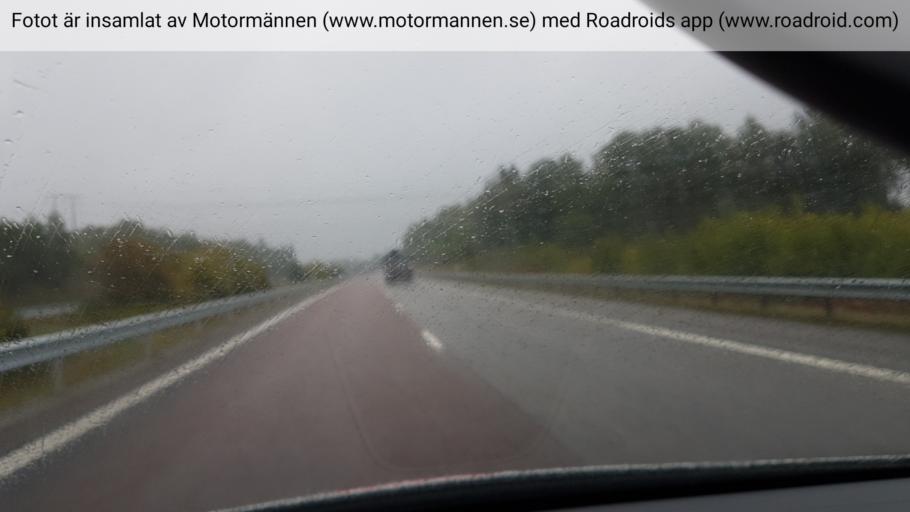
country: SE
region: Stockholm
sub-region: Nykvarns Kommun
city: Nykvarn
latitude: 59.2038
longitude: 17.3564
